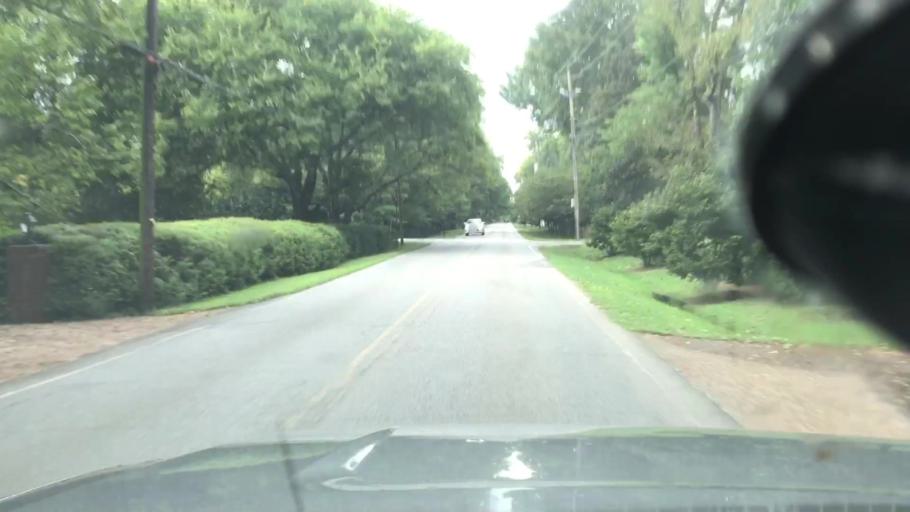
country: US
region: Tennessee
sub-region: Davidson County
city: Belle Meade
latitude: 36.0872
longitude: -86.8544
